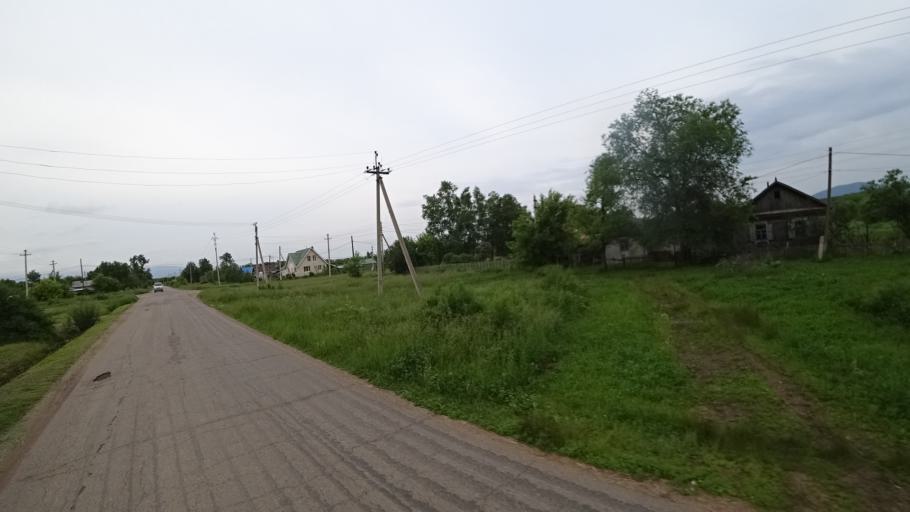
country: RU
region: Primorskiy
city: Novosysoyevka
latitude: 44.2401
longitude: 133.3685
